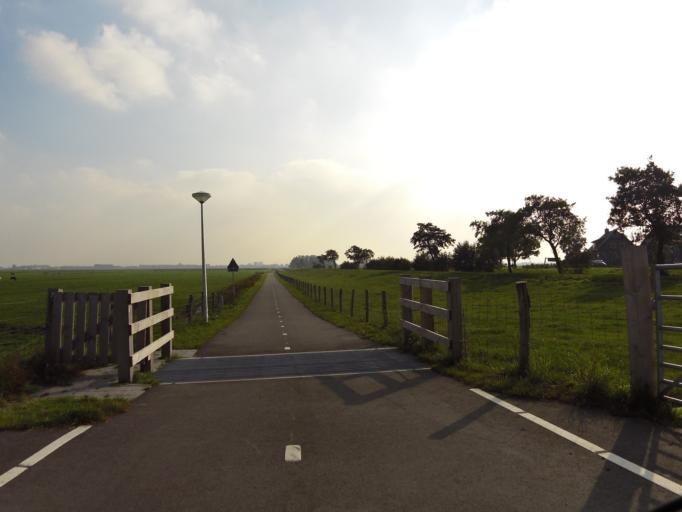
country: NL
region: South Holland
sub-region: Gemeente Rijnwoude
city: Benthuizen
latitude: 52.1047
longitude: 4.5368
